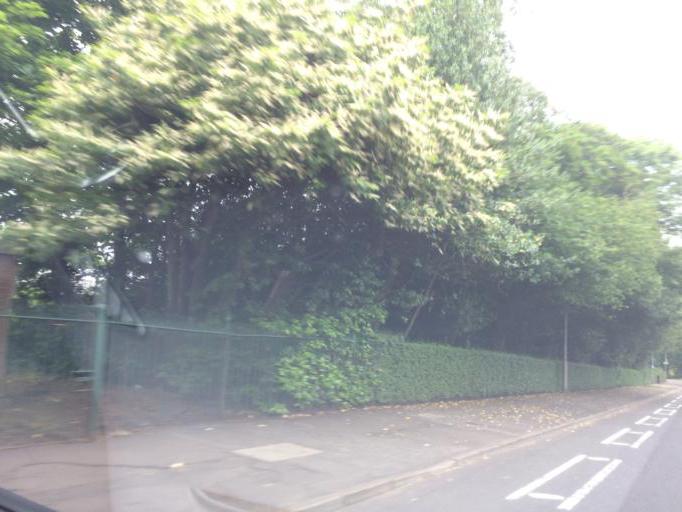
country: GB
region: Scotland
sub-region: East Renfrewshire
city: Giffnock
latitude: 55.8457
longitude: -4.3100
